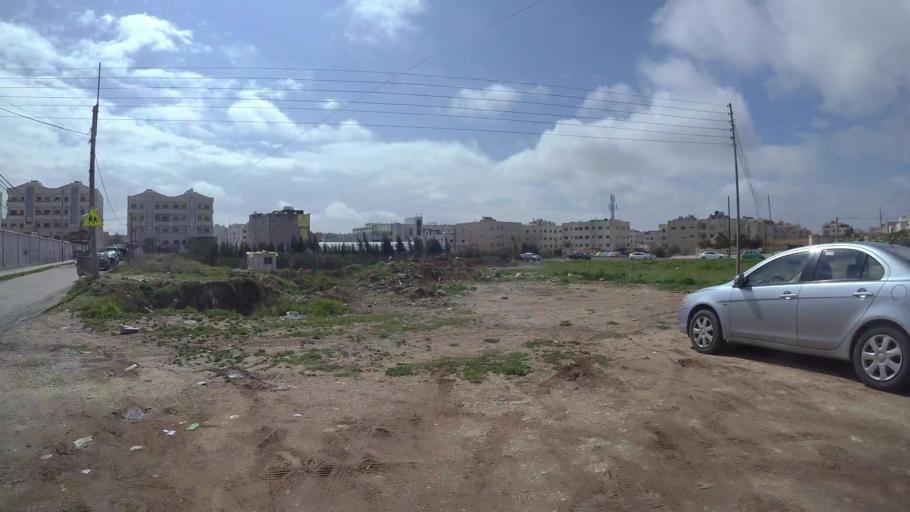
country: JO
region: Amman
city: Al Jubayhah
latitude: 31.9951
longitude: 35.8489
